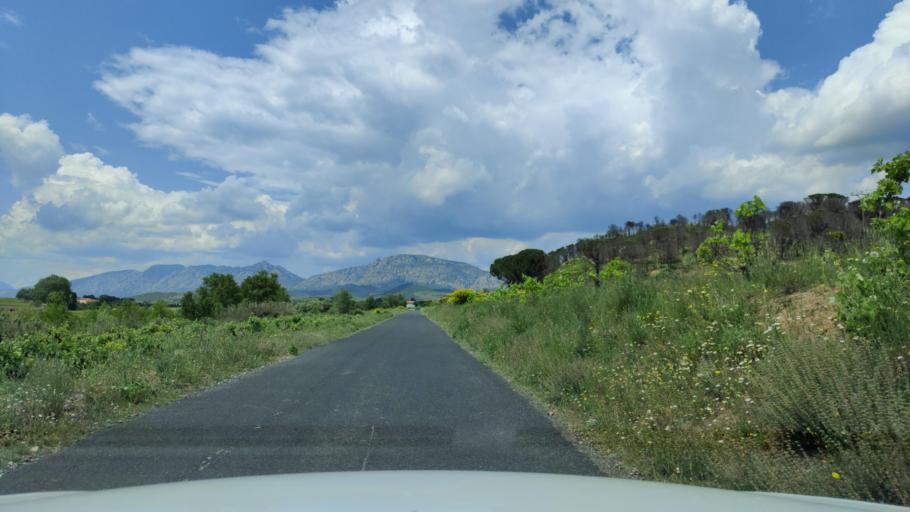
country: FR
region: Languedoc-Roussillon
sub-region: Departement des Pyrenees-Orientales
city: Estagel
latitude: 42.7899
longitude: 2.6802
